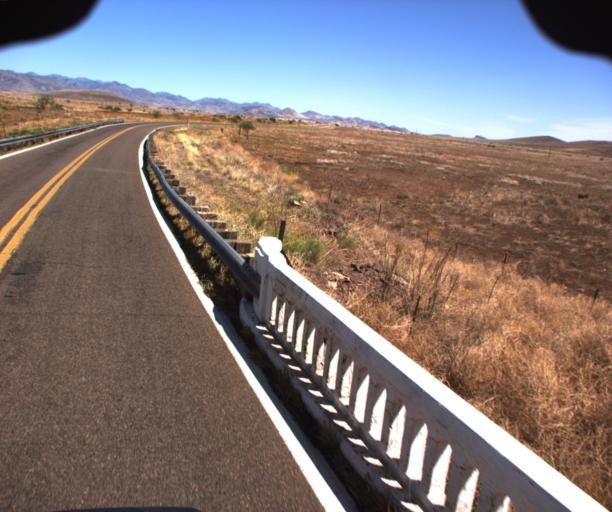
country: US
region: Arizona
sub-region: Cochise County
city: Douglas
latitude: 31.5621
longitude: -109.2654
